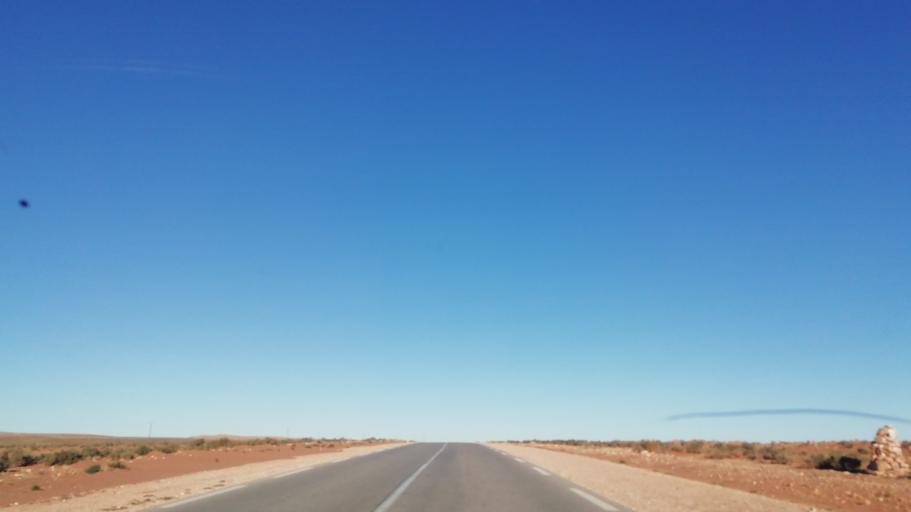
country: DZ
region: El Bayadh
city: El Abiodh Sidi Cheikh
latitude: 33.1242
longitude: 0.2794
